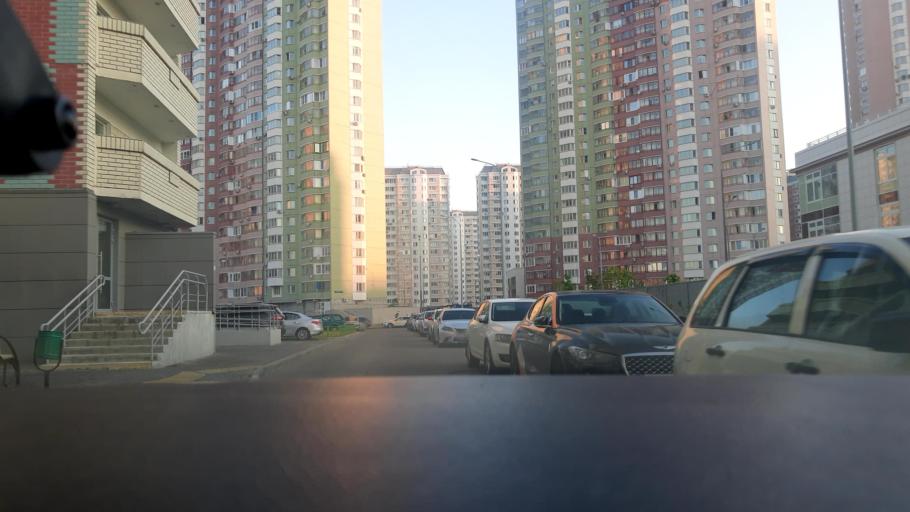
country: RU
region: Moscow
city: Nekrasovka
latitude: 55.6989
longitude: 37.9311
